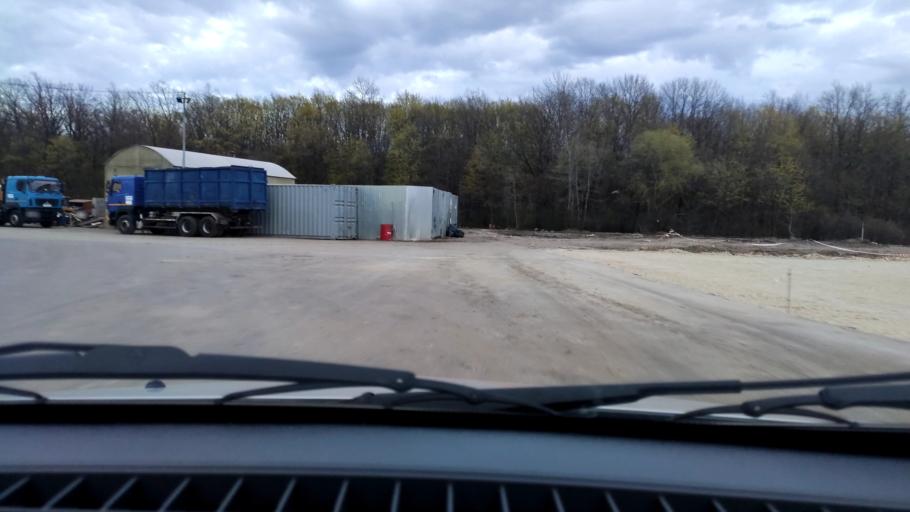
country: RU
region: Voronezj
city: Podgornoye
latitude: 51.7854
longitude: 39.2037
